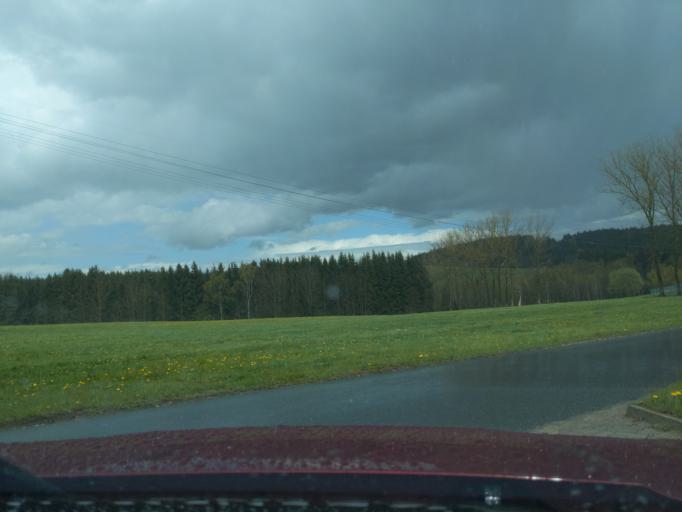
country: DE
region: Saxony
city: Schoenheide
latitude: 50.5141
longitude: 12.5221
